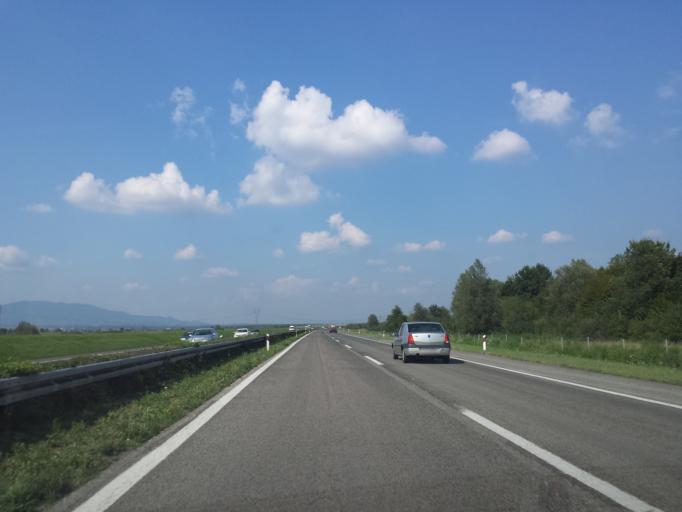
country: HR
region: Zagrebacka
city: Jastrebarsko
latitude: 45.6161
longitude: 15.6460
